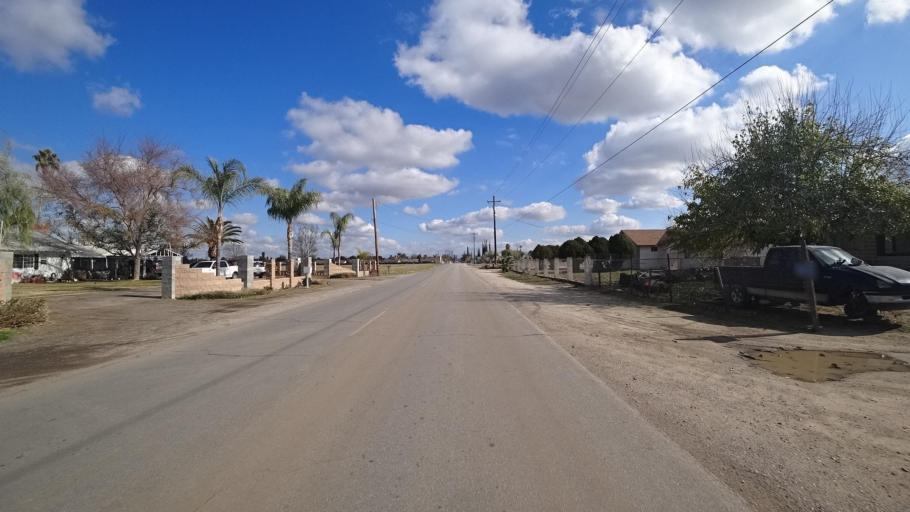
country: US
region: California
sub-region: Kern County
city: McFarland
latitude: 35.6741
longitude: -119.2441
